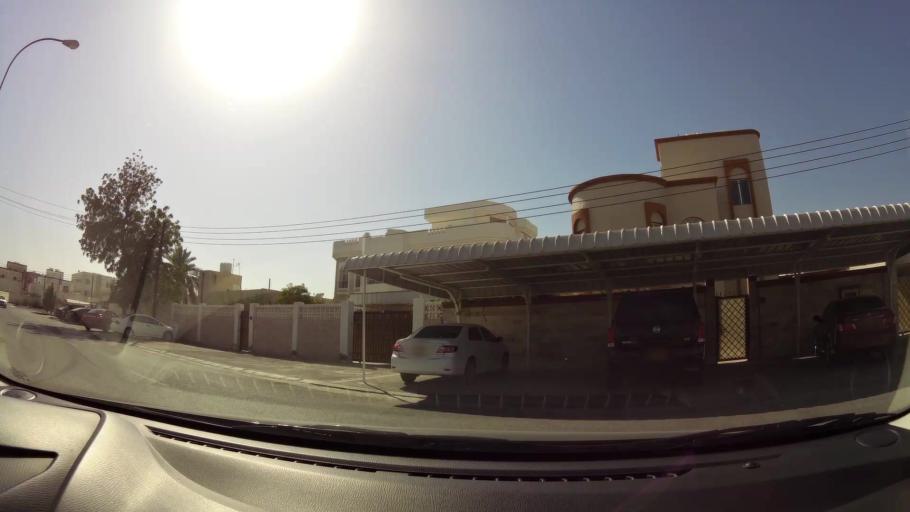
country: OM
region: Muhafazat Masqat
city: As Sib al Jadidah
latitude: 23.6291
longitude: 58.2043
